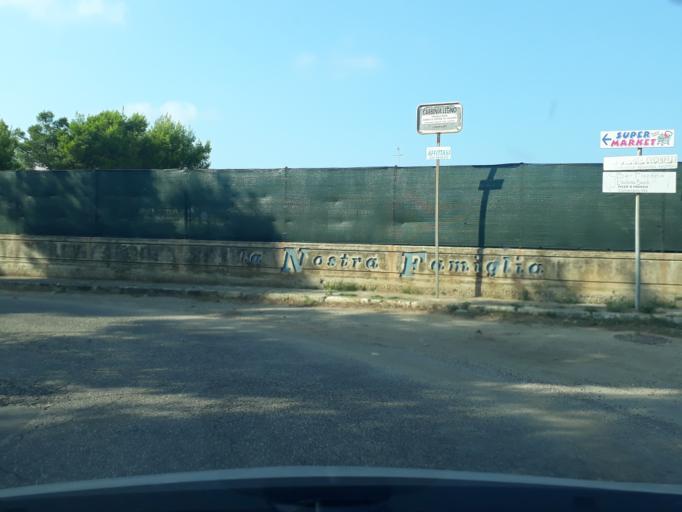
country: IT
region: Apulia
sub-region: Provincia di Brindisi
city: Carovigno
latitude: 40.7584
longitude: 17.6958
